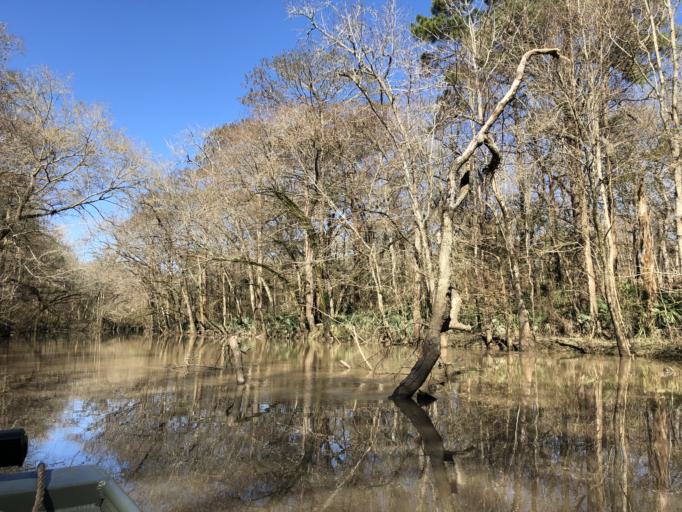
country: US
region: Louisiana
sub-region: Calcasieu Parish
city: Iowa
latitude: 30.3159
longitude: -93.0771
